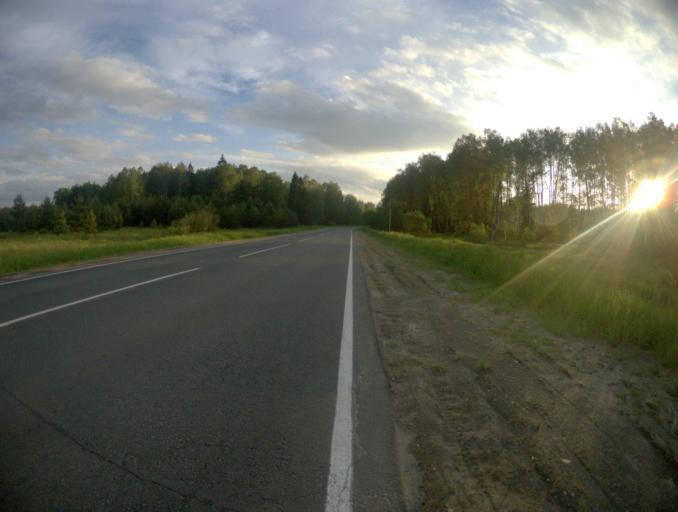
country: RU
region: Vladimir
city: Anopino
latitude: 55.6328
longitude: 40.7935
